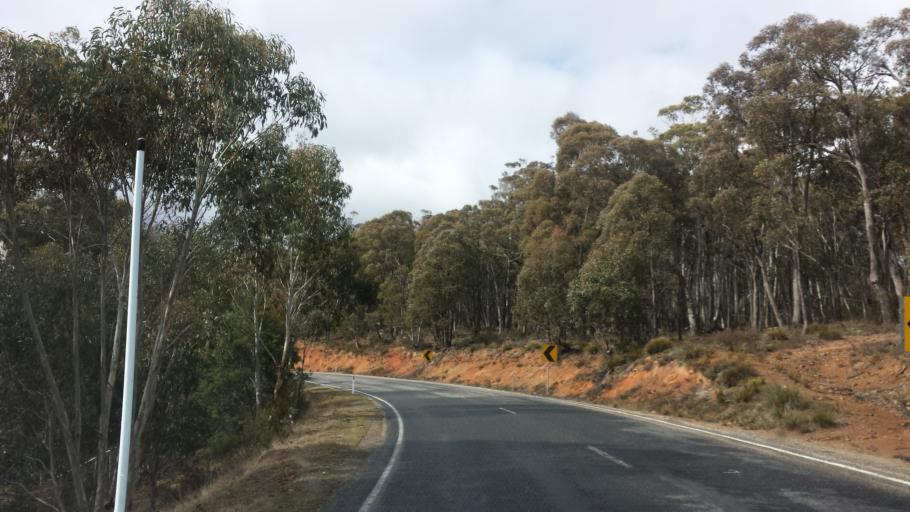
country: AU
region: Victoria
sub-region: Alpine
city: Mount Beauty
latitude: -37.0827
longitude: 147.3752
